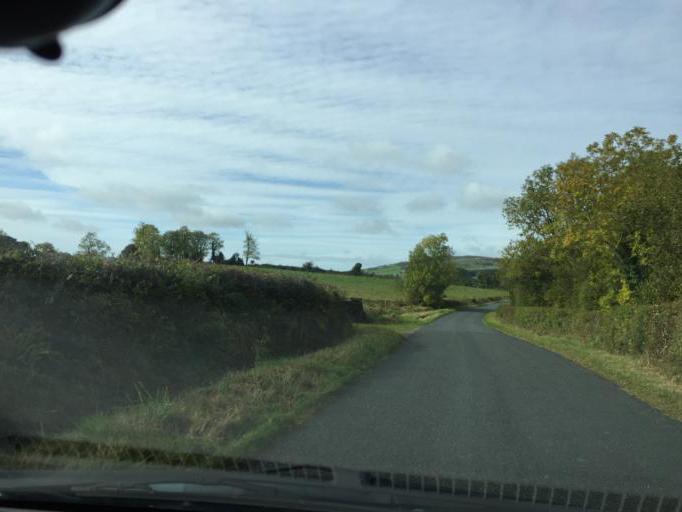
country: IE
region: Connaught
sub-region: Roscommon
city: Boyle
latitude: 54.0303
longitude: -8.3202
